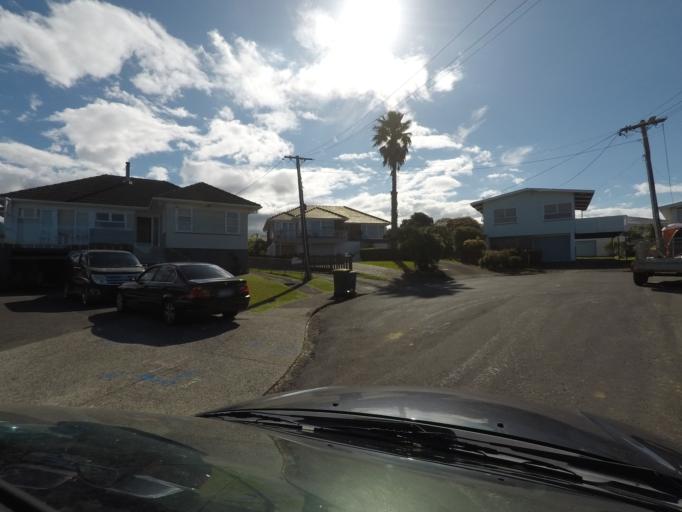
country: NZ
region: Auckland
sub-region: Auckland
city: Rosebank
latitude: -36.8700
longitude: 174.6481
